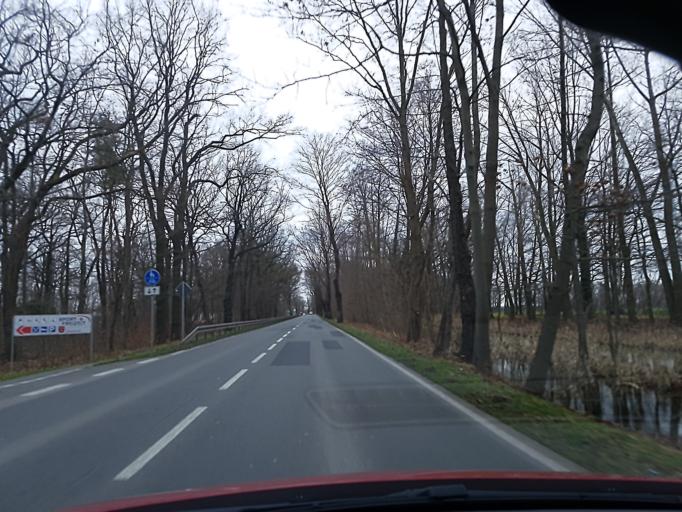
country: DE
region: Brandenburg
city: Elsterwerda
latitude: 51.4474
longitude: 13.5161
